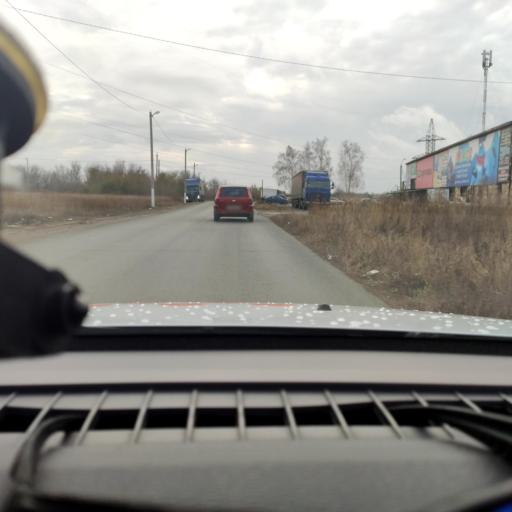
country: RU
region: Samara
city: Chapayevsk
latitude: 52.9939
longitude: 49.7325
